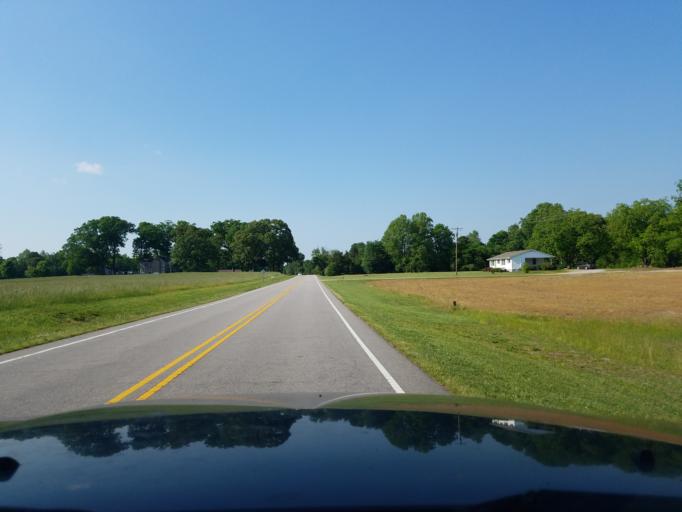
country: US
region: North Carolina
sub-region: Vance County
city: Henderson
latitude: 36.3957
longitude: -78.3684
